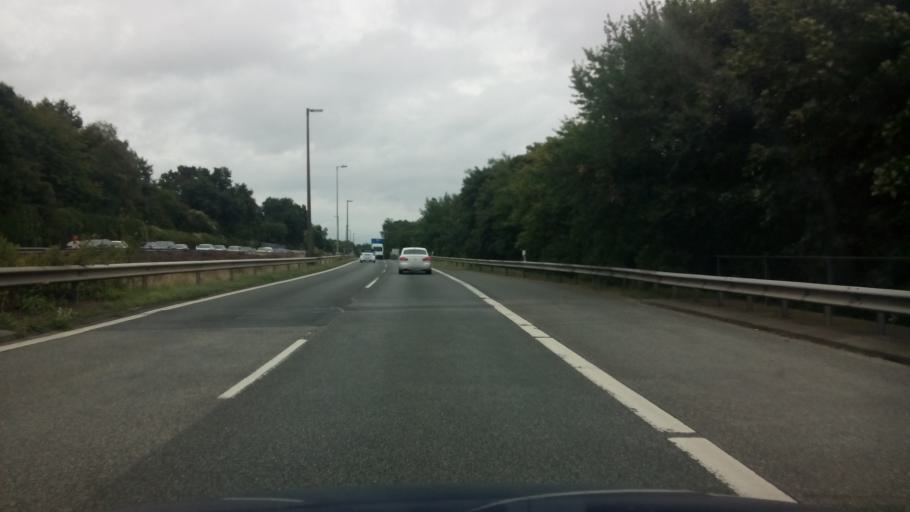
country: DE
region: Lower Saxony
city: Ritterhude
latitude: 53.1760
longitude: 8.7051
